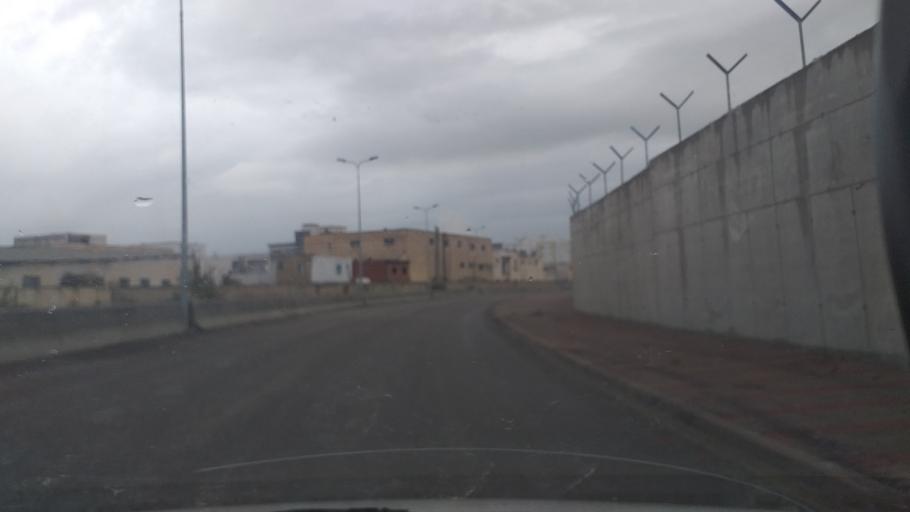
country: TN
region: Ariana
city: Ariana
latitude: 36.8601
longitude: 10.2148
